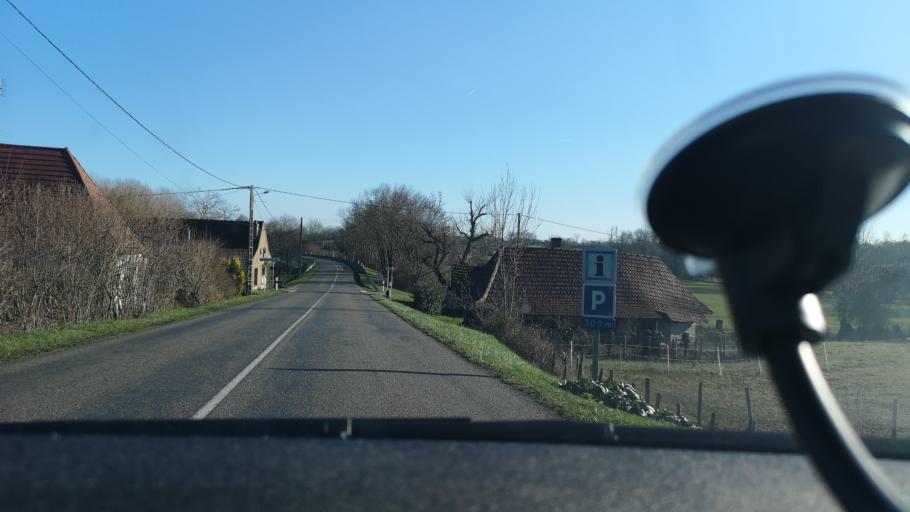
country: FR
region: Bourgogne
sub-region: Departement de Saone-et-Loire
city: Saint-Germain-du-Bois
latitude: 46.7496
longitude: 5.2893
